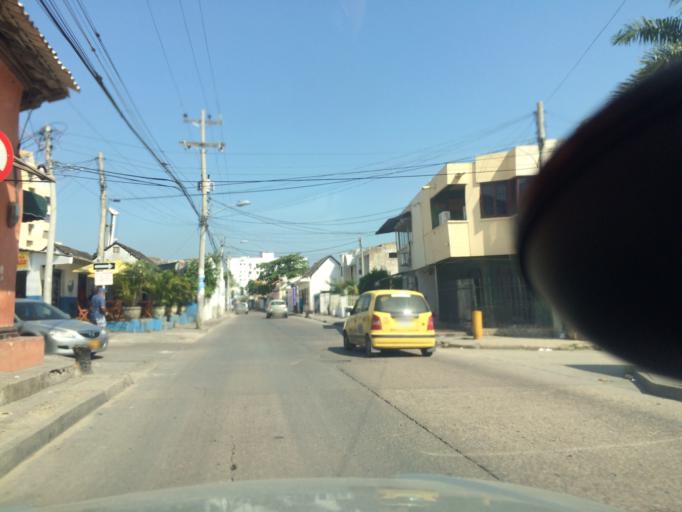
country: CO
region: Bolivar
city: Cartagena
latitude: 10.4166
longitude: -75.5365
